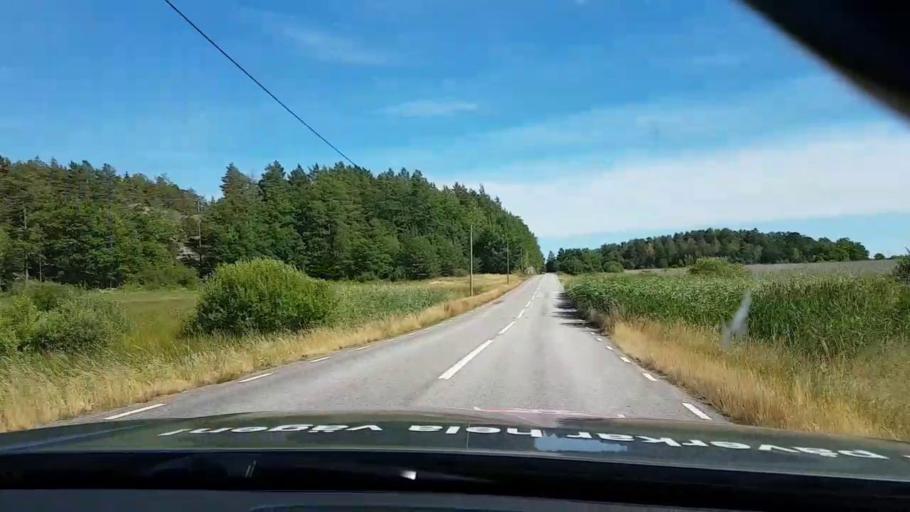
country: SE
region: Kalmar
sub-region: Vasterviks Kommun
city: Forserum
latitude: 57.9241
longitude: 16.5609
